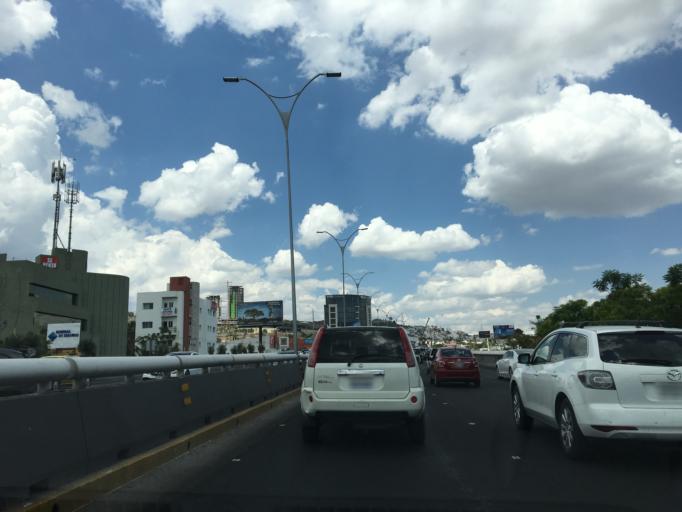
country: MX
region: Queretaro
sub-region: Queretaro
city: Santiago de Queretaro
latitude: 20.6166
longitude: -100.3931
